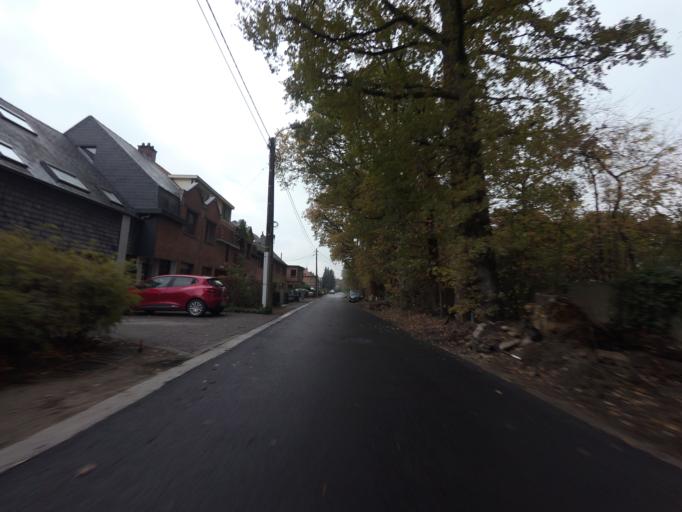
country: BE
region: Flanders
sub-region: Provincie Antwerpen
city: Bonheiden
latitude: 51.0162
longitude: 4.5543
